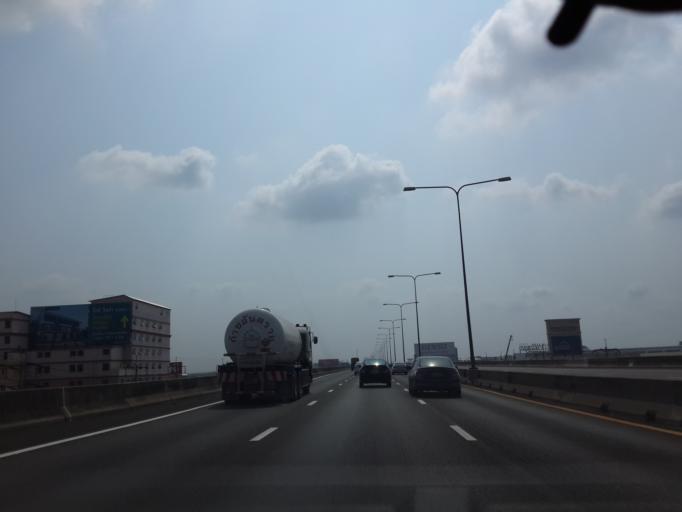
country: TH
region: Bangkok
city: Bang Na
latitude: 13.6349
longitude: 100.7093
